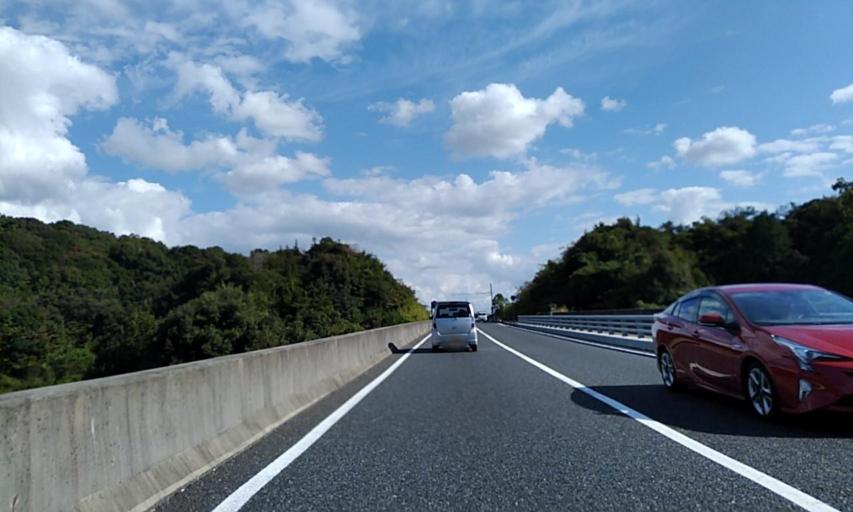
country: JP
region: Wakayama
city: Tanabe
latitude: 33.7487
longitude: 135.3623
